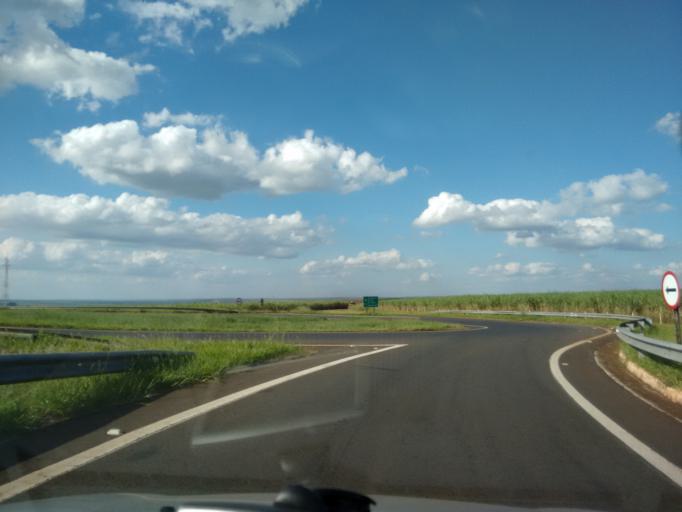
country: BR
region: Sao Paulo
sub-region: Americo Brasiliense
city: Americo Brasiliense
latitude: -21.6246
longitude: -47.9644
